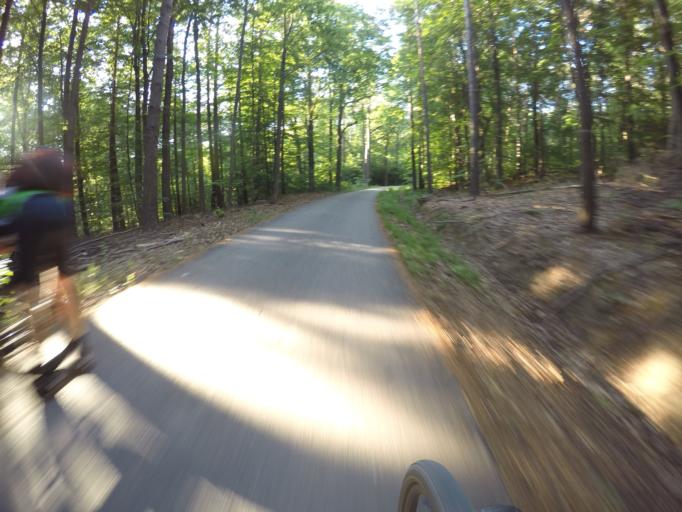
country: DE
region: Baden-Wuerttemberg
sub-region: Regierungsbezirk Stuttgart
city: Fellbach
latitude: 48.7819
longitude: 9.3064
